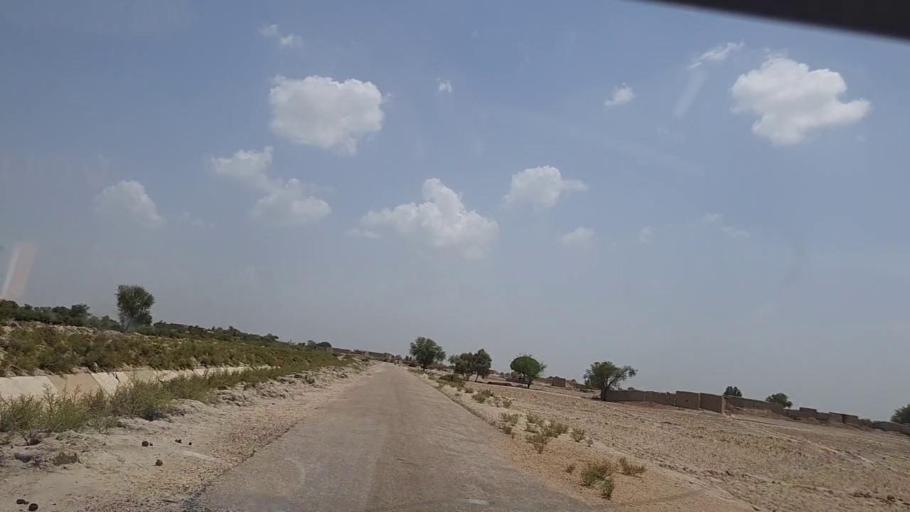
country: PK
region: Sindh
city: Bhan
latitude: 26.5247
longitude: 67.6345
